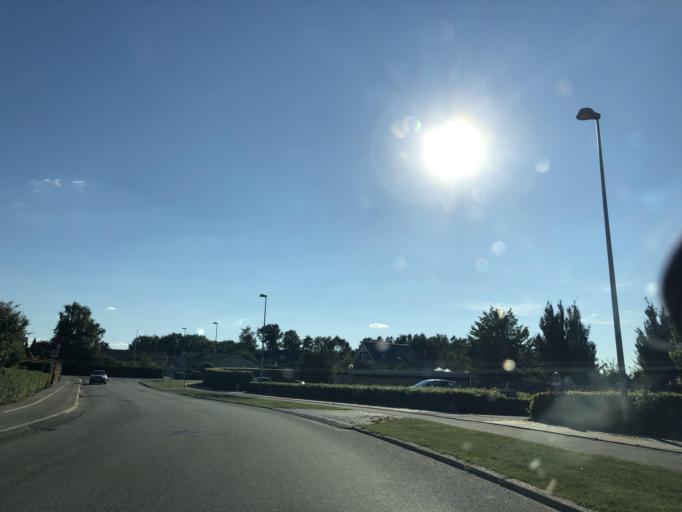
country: DK
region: North Denmark
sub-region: Mariagerfjord Kommune
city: Hobro
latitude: 56.6333
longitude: 9.8130
